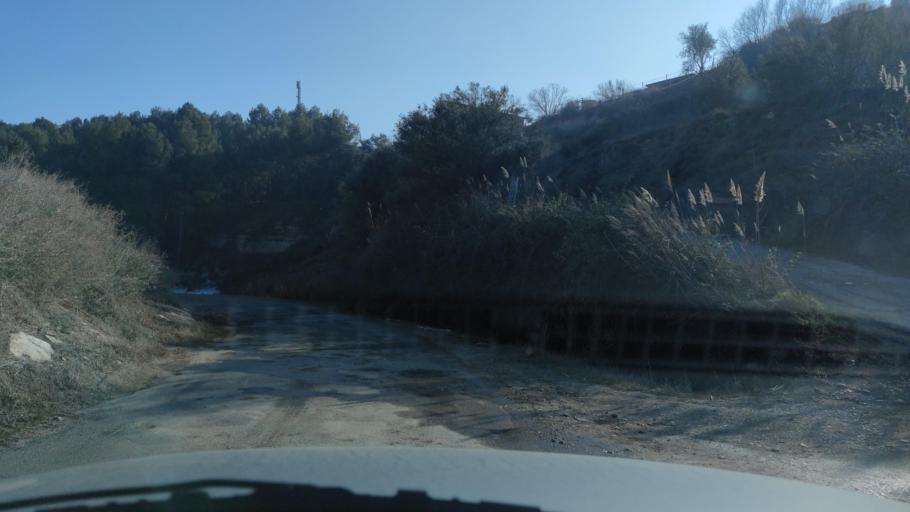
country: ES
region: Catalonia
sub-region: Provincia de Lleida
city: Seros
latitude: 41.4642
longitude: 0.4017
